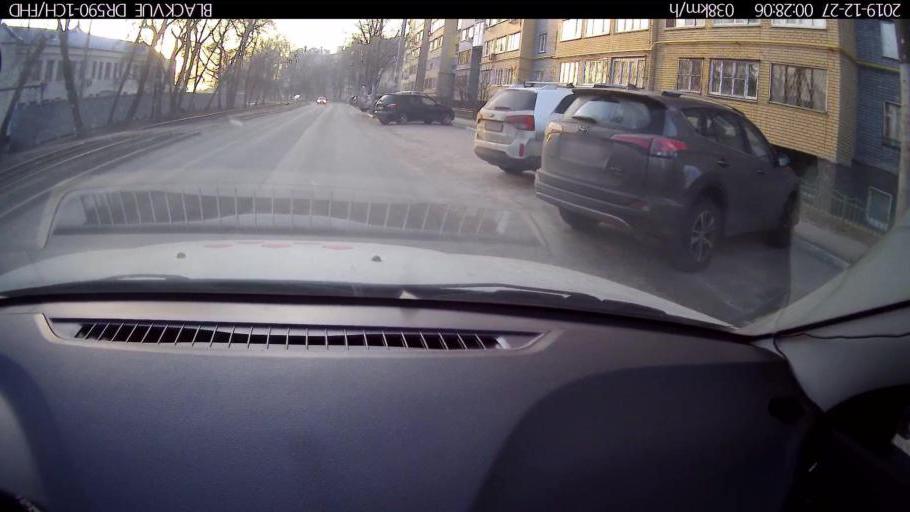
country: RU
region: Nizjnij Novgorod
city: Nizhniy Novgorod
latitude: 56.3134
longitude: 43.9323
